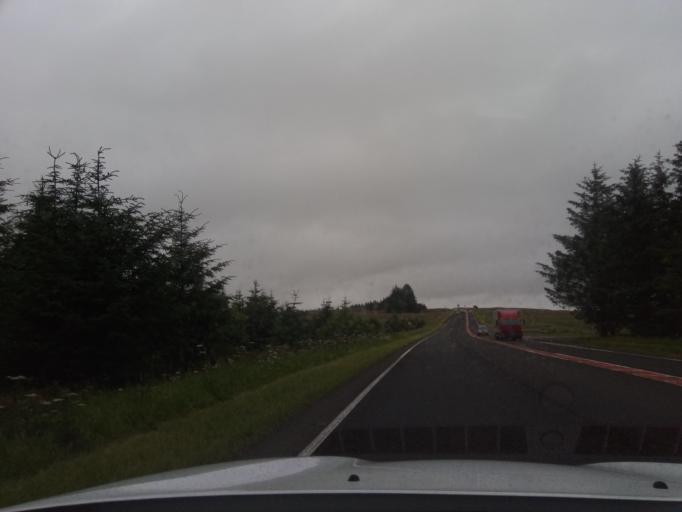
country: GB
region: Scotland
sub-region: East Lothian
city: Pencaitland
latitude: 55.8180
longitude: -2.8476
